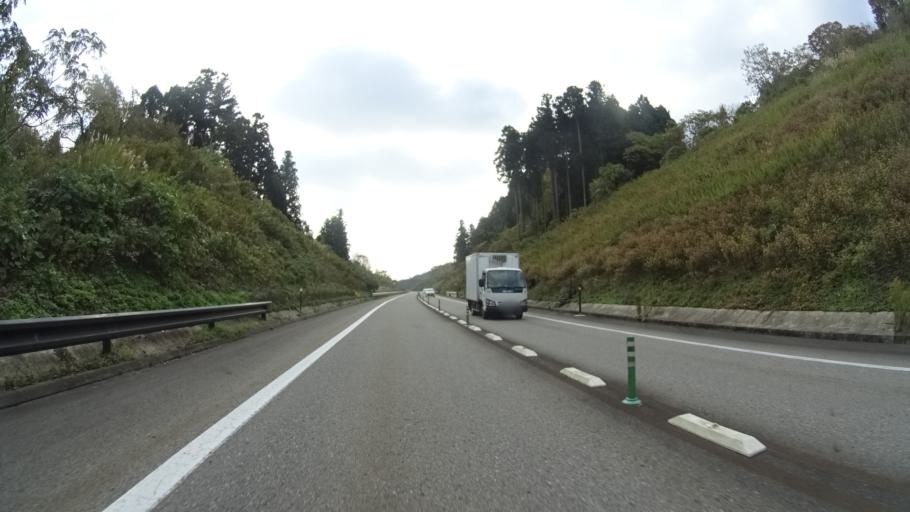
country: JP
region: Ishikawa
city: Nanao
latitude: 37.0102
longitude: 137.0322
